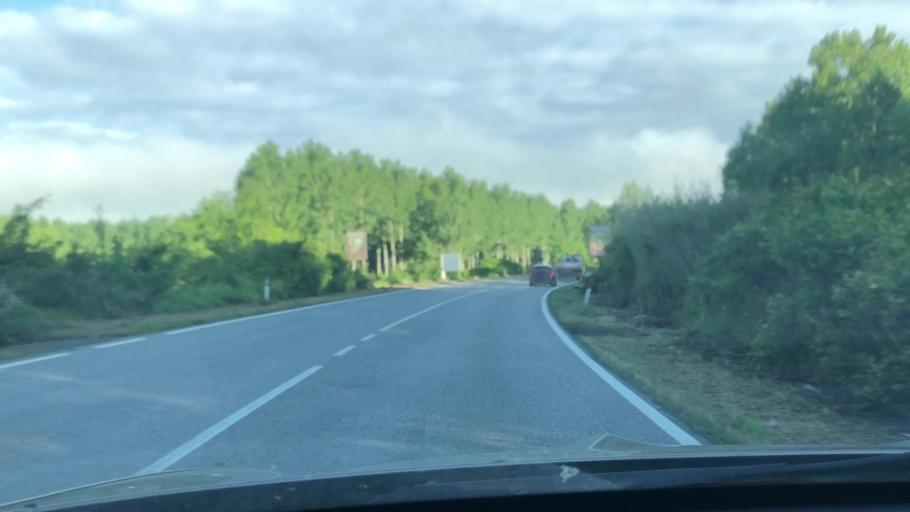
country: IT
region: Tuscany
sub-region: Province of Pisa
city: Forcoli
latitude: 43.6053
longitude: 10.6911
